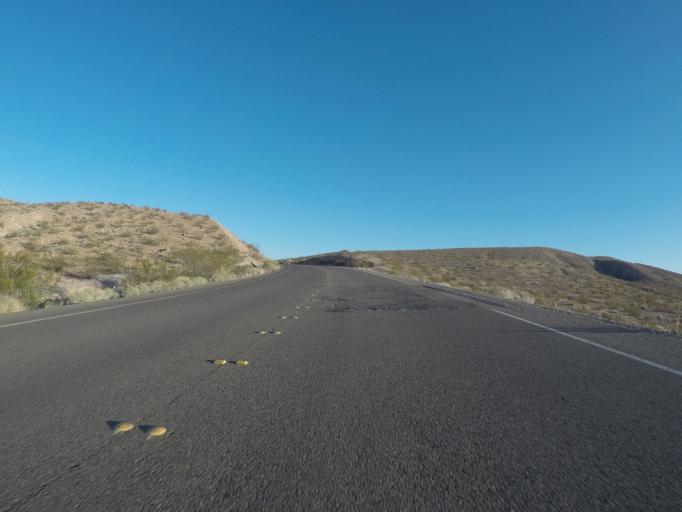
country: US
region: Nevada
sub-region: Clark County
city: Moapa Valley
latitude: 36.2761
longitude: -114.4870
